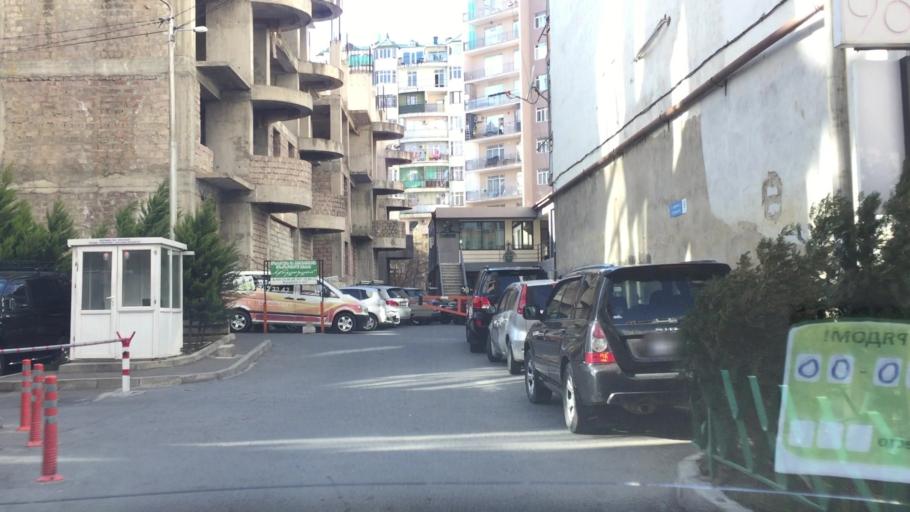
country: GE
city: Tsqnet'i
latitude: 41.7134
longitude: 44.7603
